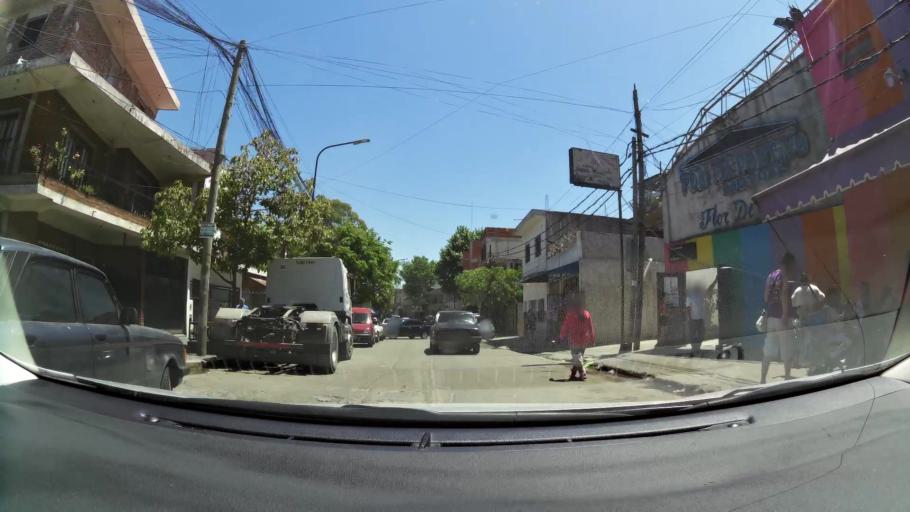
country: AR
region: Buenos Aires
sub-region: Partido de Avellaneda
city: Avellaneda
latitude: -34.6544
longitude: -58.4025
